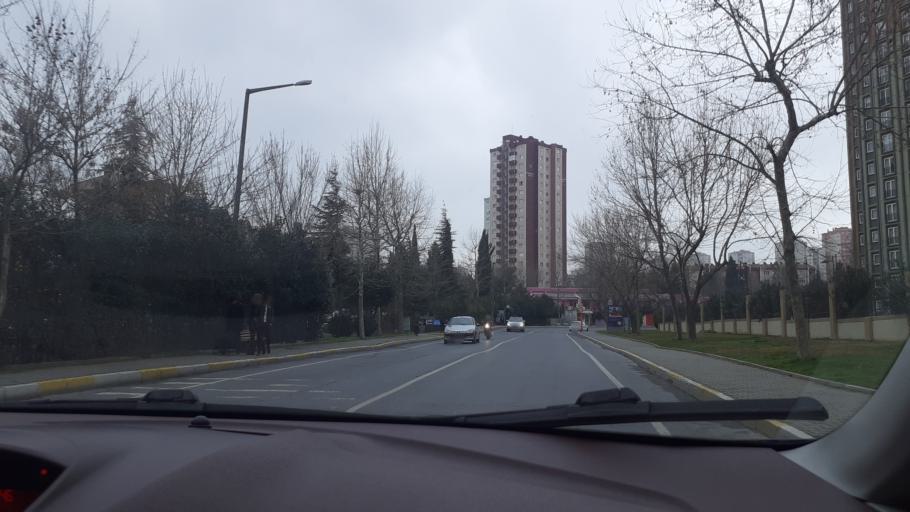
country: TR
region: Istanbul
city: Mahmutbey
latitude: 41.0512
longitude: 28.7877
